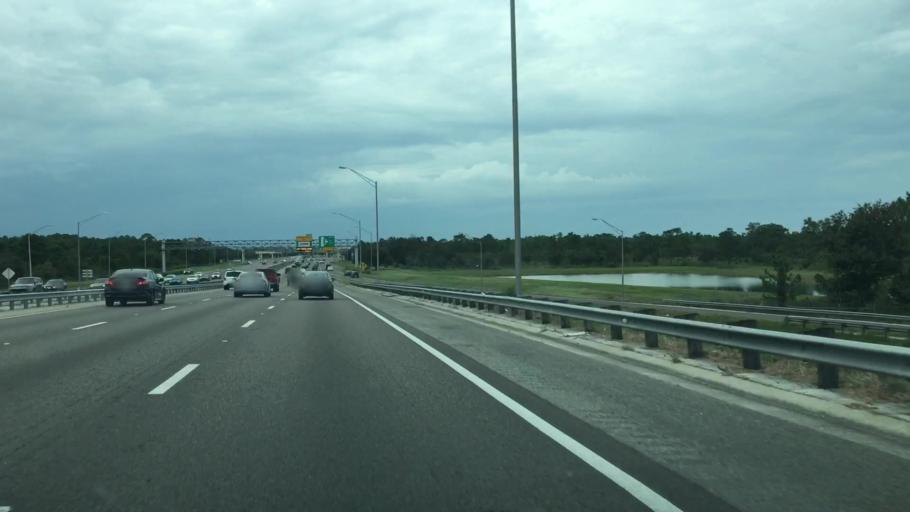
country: US
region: Florida
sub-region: Orange County
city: Azalea Park
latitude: 28.4797
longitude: -81.2398
